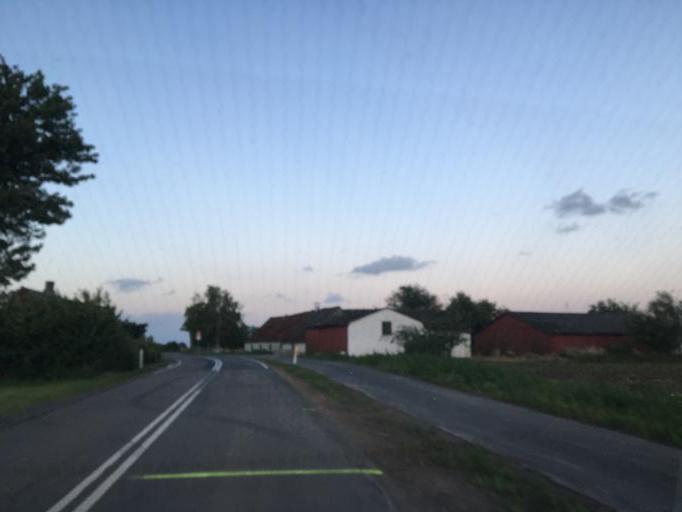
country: DK
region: Zealand
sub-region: Solrod Kommune
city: Havdrup
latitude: 55.5188
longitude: 12.1393
